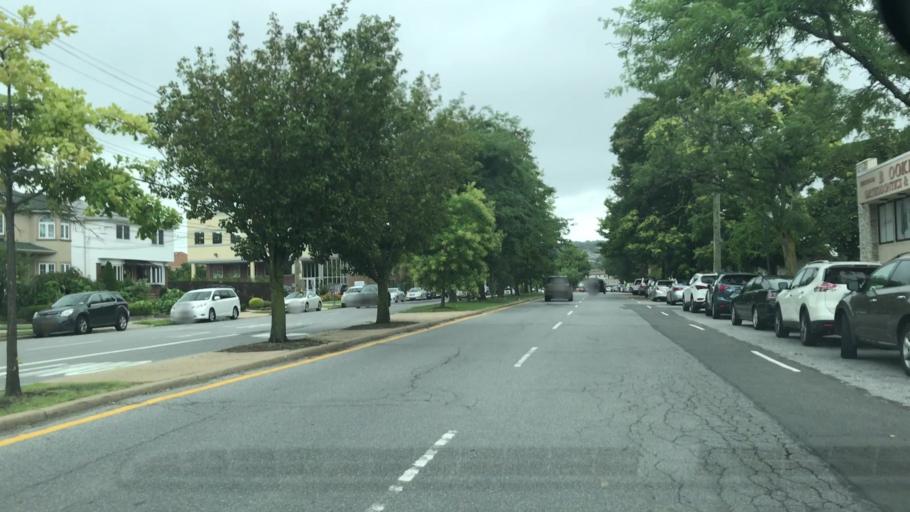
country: US
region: New York
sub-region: Richmond County
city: Staten Island
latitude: 40.5849
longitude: -74.0887
